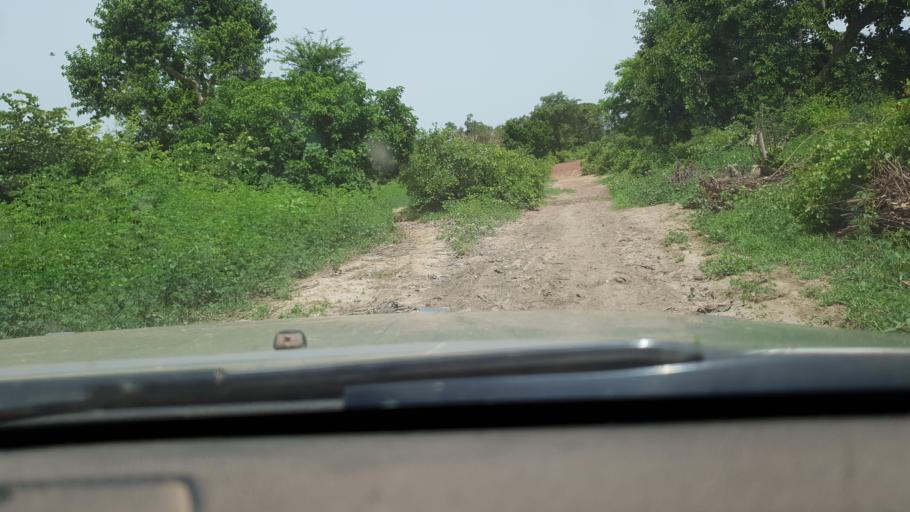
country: ML
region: Koulikoro
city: Koulikoro
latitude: 12.6638
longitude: -7.2112
